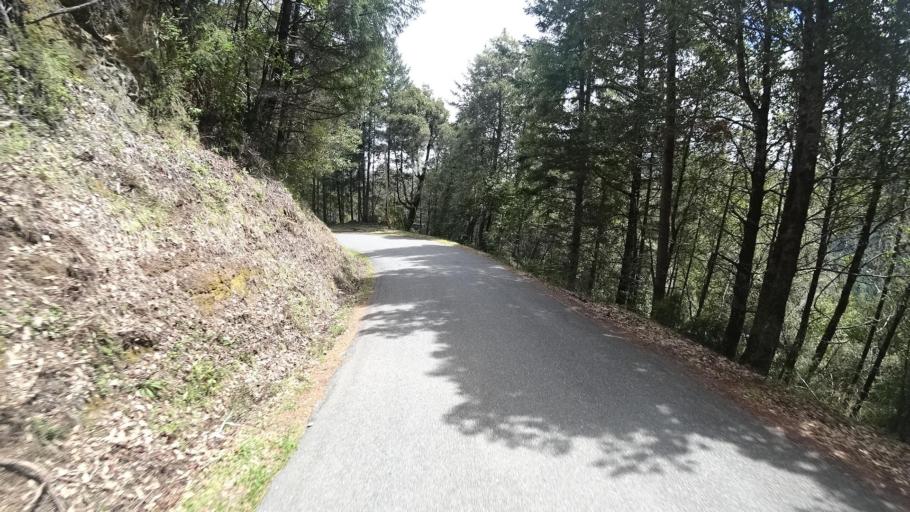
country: US
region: California
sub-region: Humboldt County
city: Blue Lake
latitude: 40.7582
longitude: -123.9199
